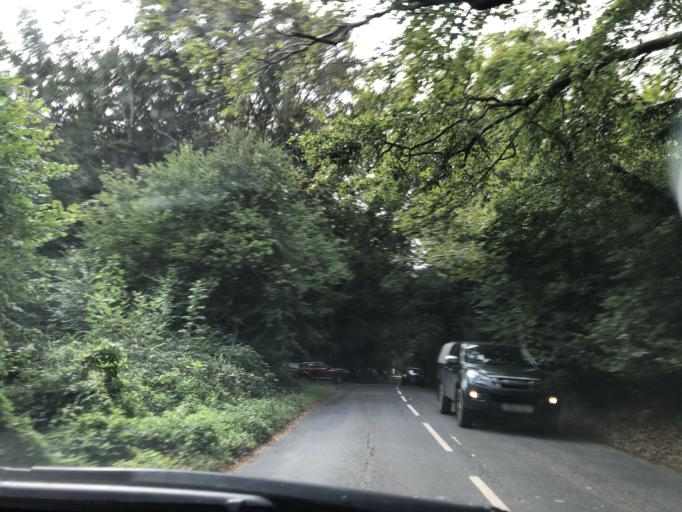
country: GB
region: England
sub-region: East Sussex
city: Forest Row
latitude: 51.0801
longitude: 0.0695
